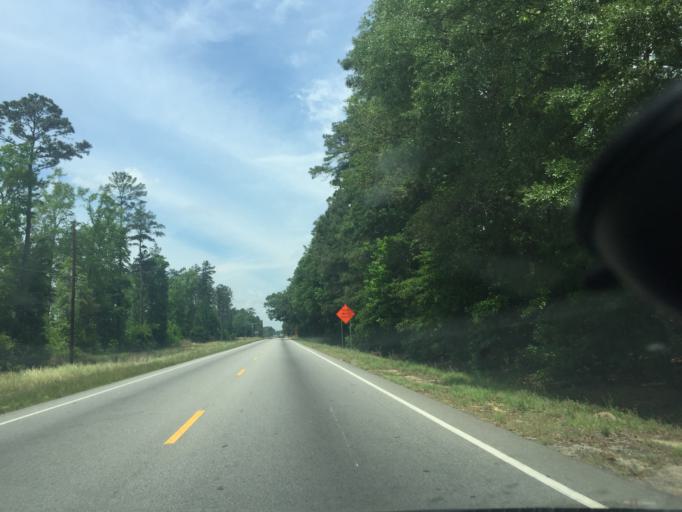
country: US
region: Georgia
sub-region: Chatham County
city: Bloomingdale
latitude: 32.1564
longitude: -81.3608
